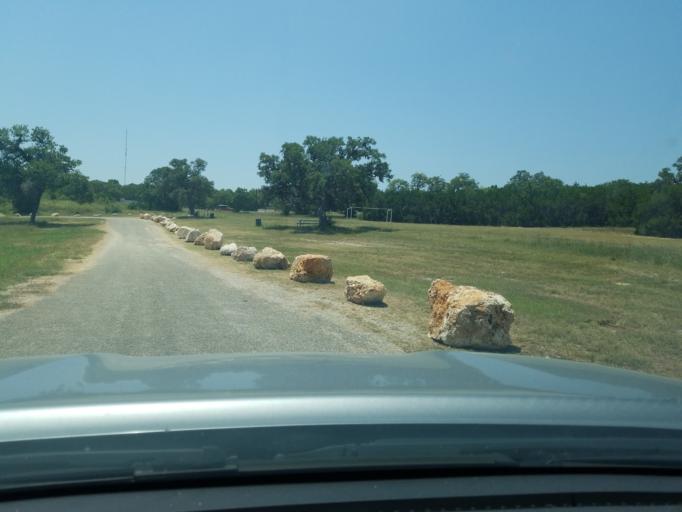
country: US
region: Texas
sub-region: Bexar County
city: Timberwood Park
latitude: 29.7088
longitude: -98.5157
